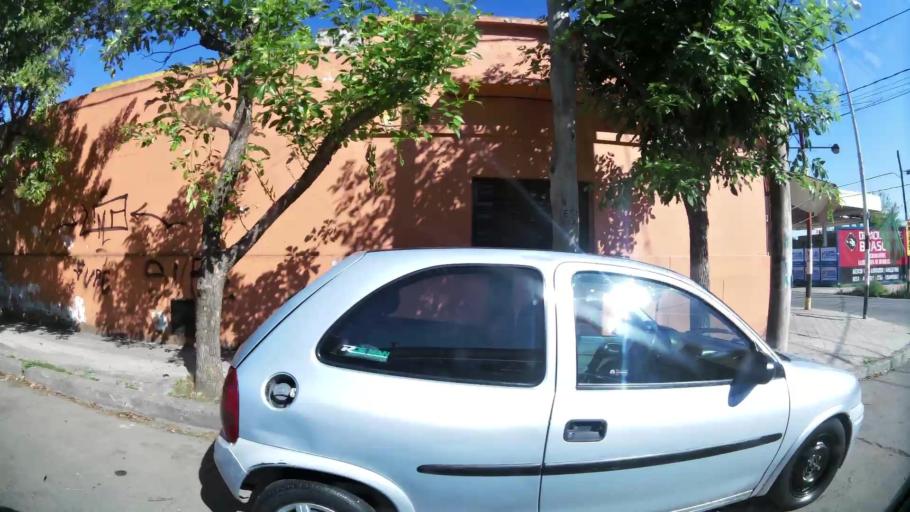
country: AR
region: Cordoba
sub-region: Departamento de Capital
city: Cordoba
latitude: -31.4387
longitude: -64.1632
